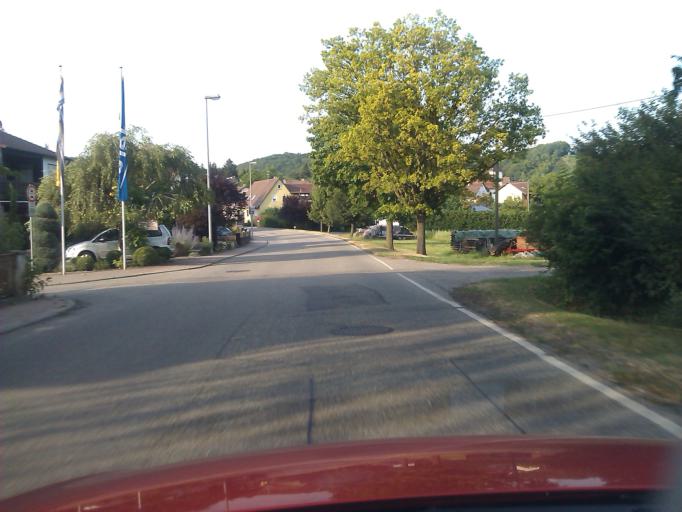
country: DE
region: Baden-Wuerttemberg
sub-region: Regierungsbezirk Stuttgart
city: Zaberfeld
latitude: 49.0695
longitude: 8.9408
